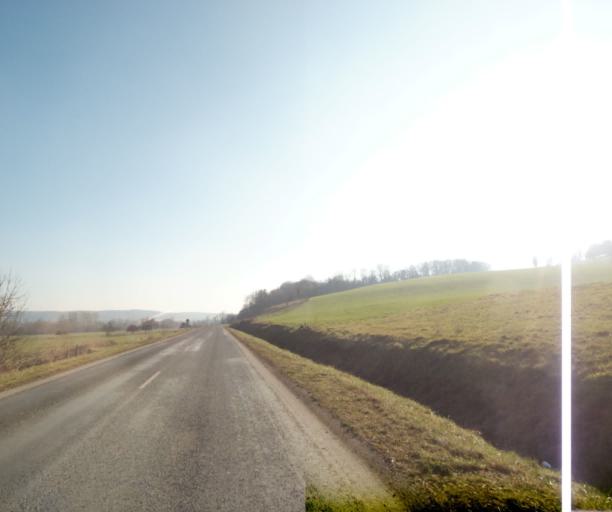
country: FR
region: Champagne-Ardenne
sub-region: Departement de la Haute-Marne
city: Chevillon
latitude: 48.5033
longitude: 5.1161
